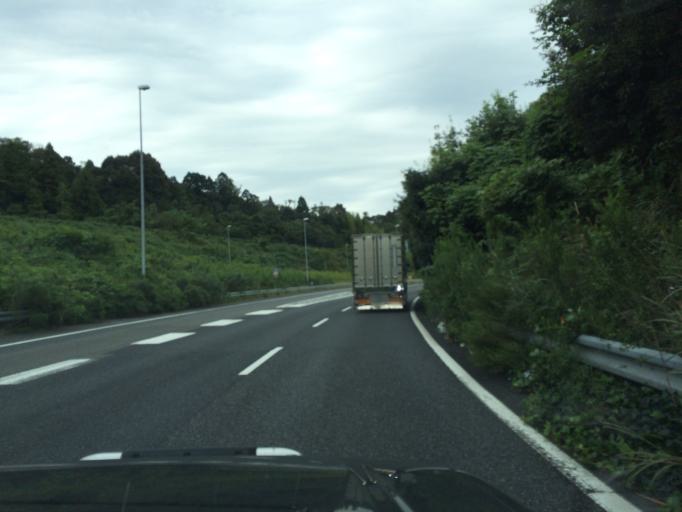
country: JP
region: Mie
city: Kameyama
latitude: 34.8621
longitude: 136.4128
